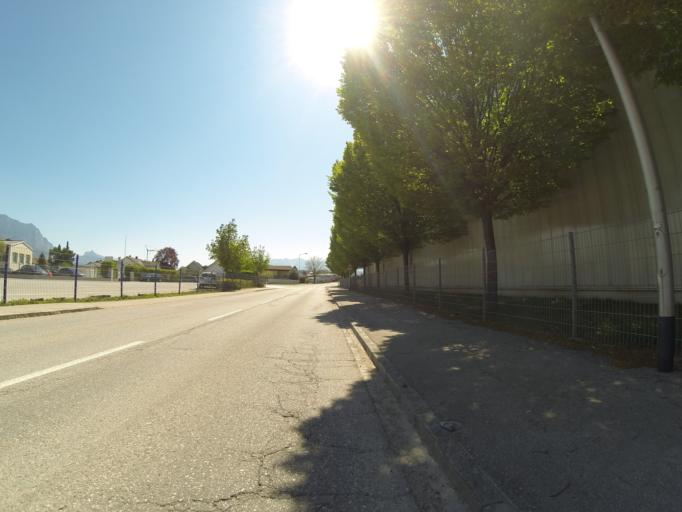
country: AT
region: Upper Austria
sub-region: Politischer Bezirk Gmunden
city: Gmunden
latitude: 47.9315
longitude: 13.7901
